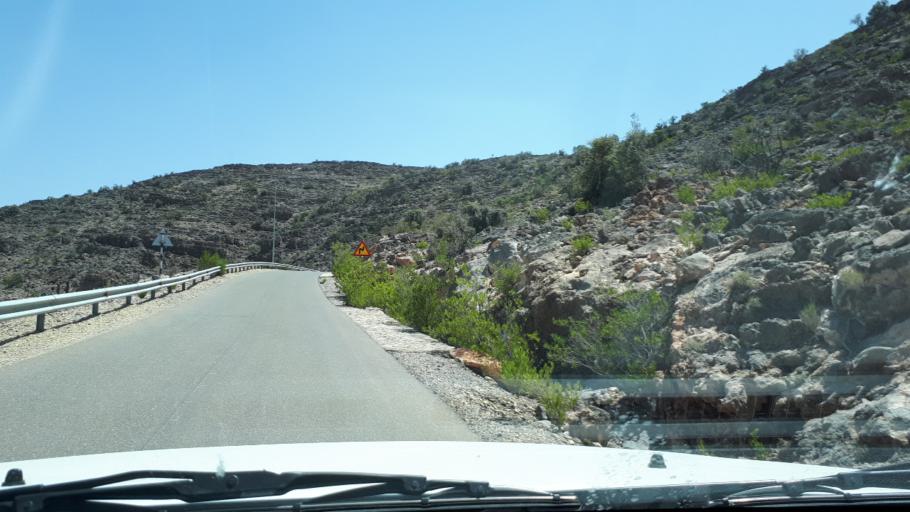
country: OM
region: Muhafazat ad Dakhiliyah
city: Izki
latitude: 23.0782
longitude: 57.7164
